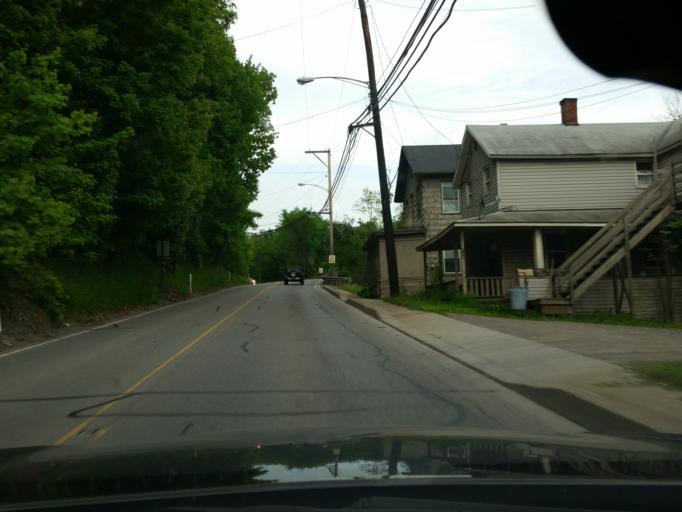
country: US
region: Pennsylvania
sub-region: Elk County
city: Ridgway
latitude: 41.4224
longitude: -78.7254
